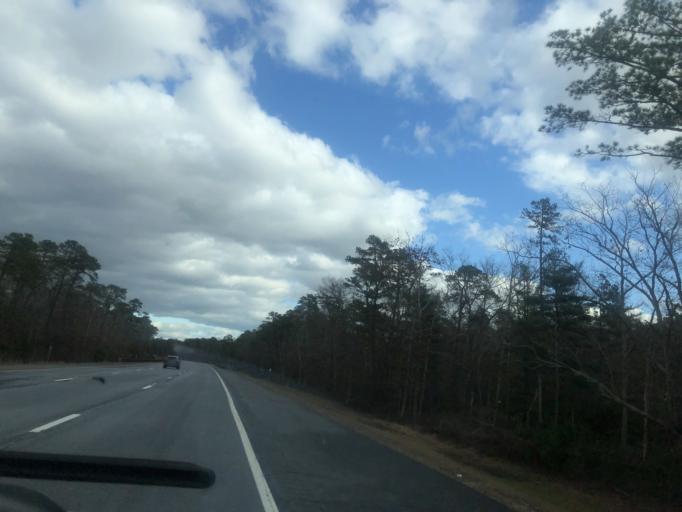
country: US
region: New Jersey
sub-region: Ocean County
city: Tuckerton
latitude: 39.6188
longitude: -74.4078
